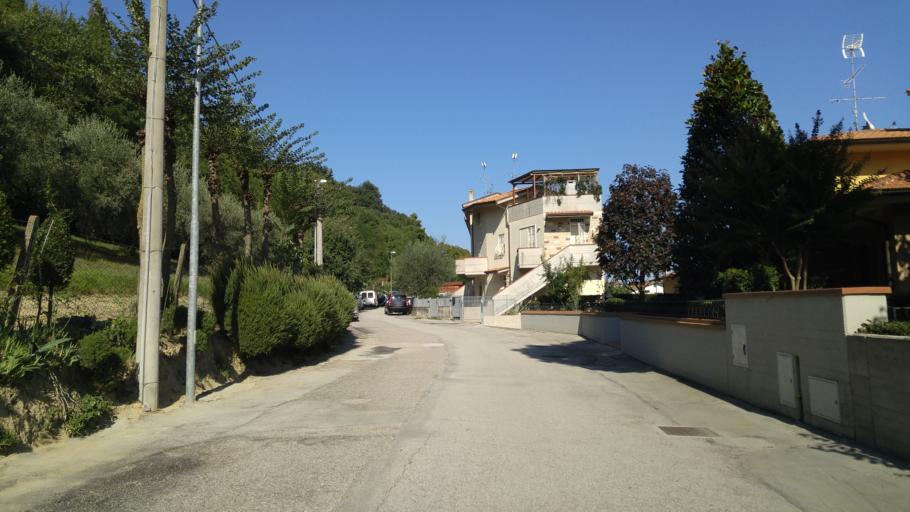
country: IT
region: The Marches
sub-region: Provincia di Pesaro e Urbino
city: Cuccurano
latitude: 43.8057
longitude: 12.9769
